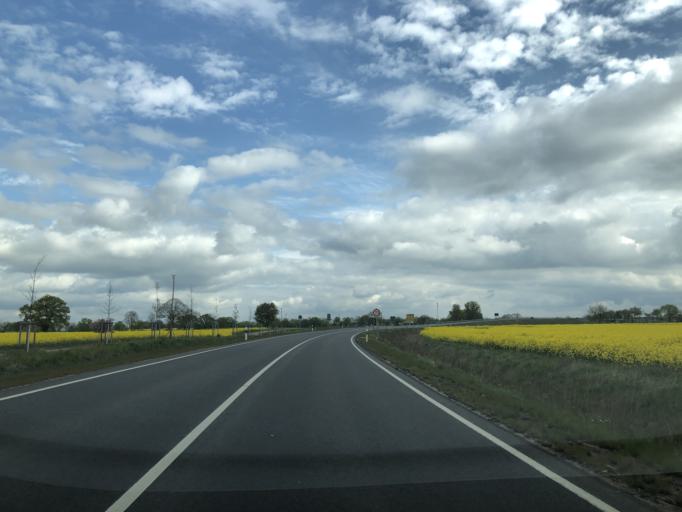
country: DE
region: Mecklenburg-Vorpommern
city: Plau am See
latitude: 53.4660
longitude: 12.2501
